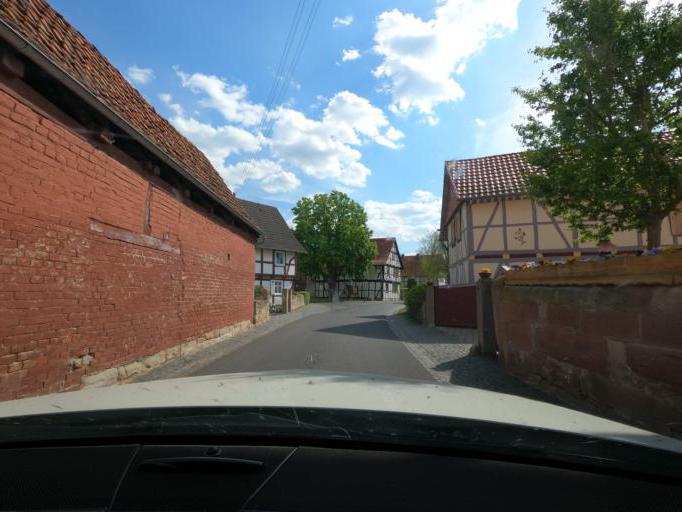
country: DE
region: Hesse
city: Wanfried
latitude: 51.1507
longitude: 10.1780
